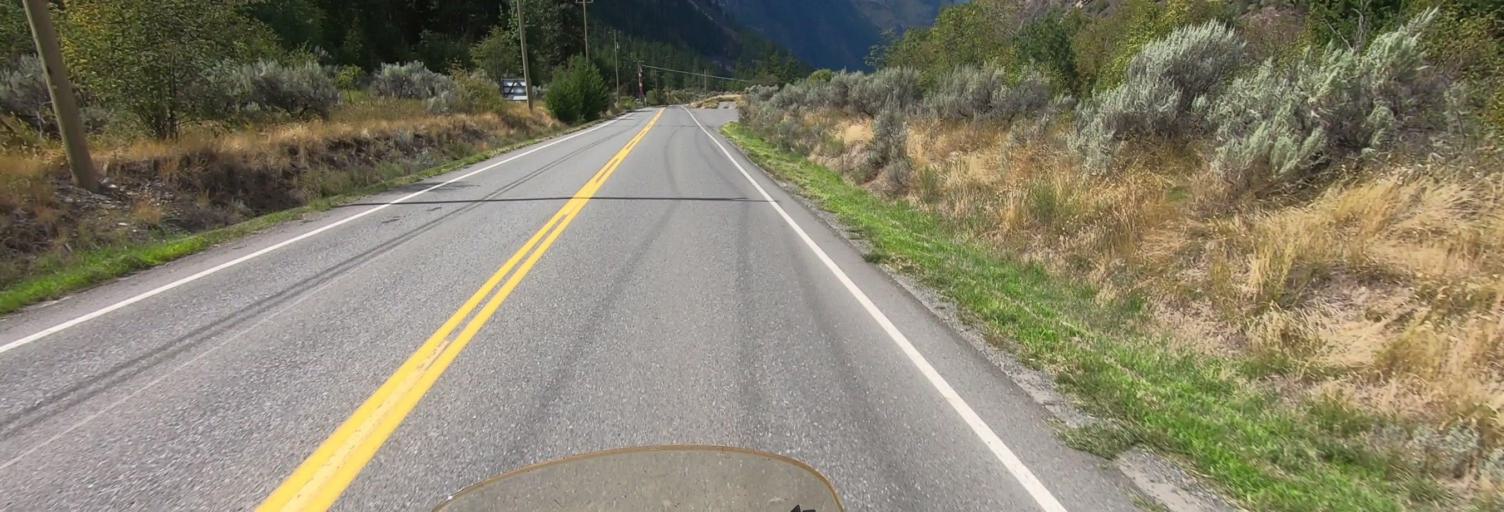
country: CA
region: British Columbia
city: Lillooet
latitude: 50.6706
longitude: -121.9451
